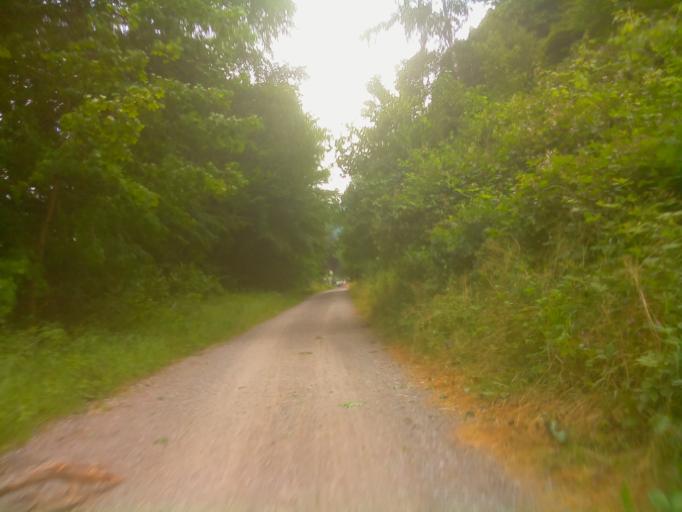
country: DE
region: Hesse
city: Hirschhorn
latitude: 49.4392
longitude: 8.8993
